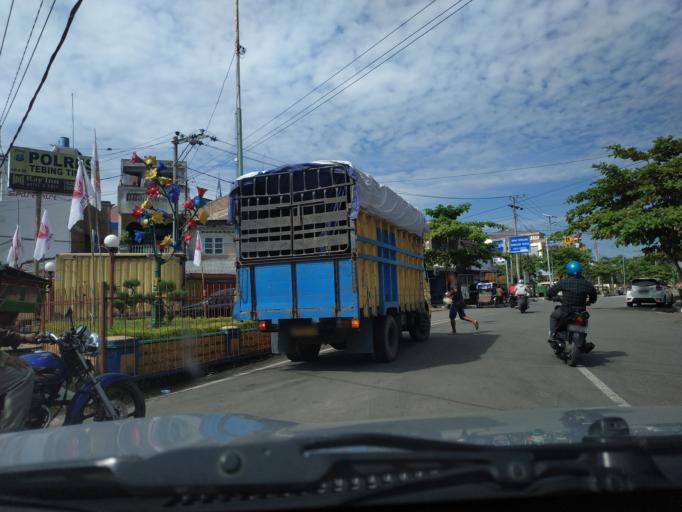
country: ID
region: North Sumatra
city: Tebingtinggi
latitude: 3.3269
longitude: 99.1679
